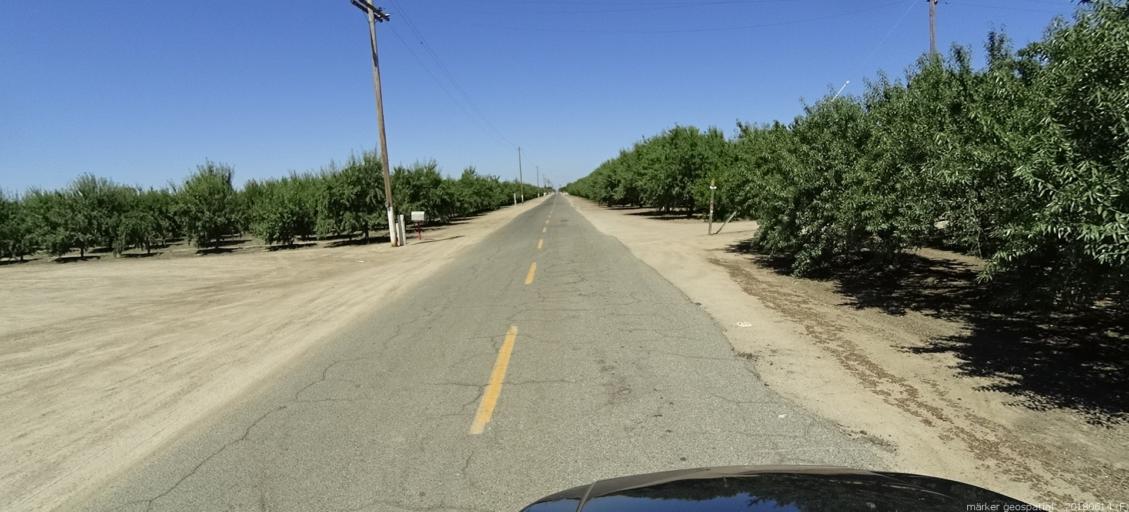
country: US
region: California
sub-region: Madera County
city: Fairmead
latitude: 36.9892
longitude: -120.1726
